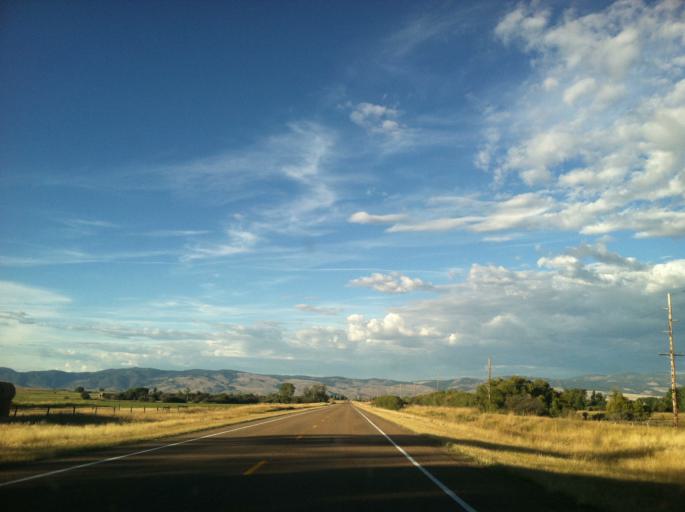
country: US
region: Montana
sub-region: Granite County
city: Philipsburg
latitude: 46.5646
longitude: -113.2106
